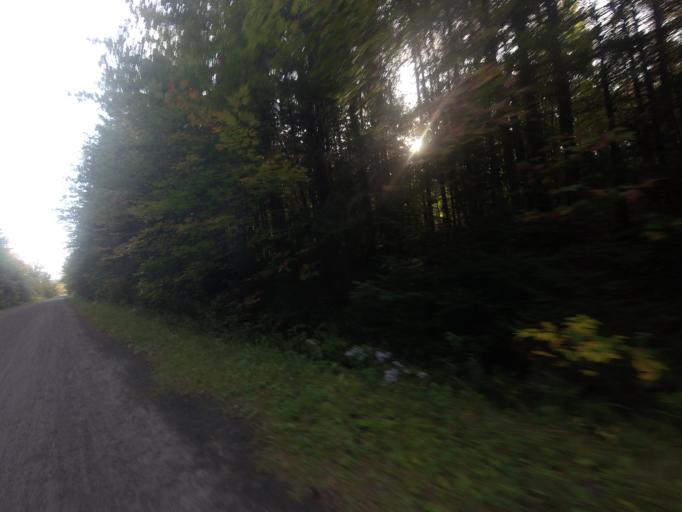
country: CA
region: Quebec
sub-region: Laurentides
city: Sainte-Adele
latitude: 45.9545
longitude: -74.1107
